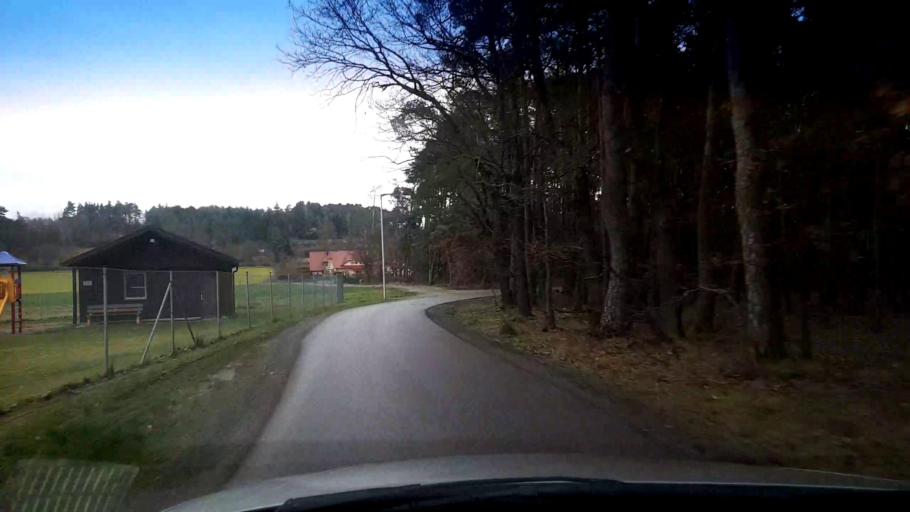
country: DE
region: Bavaria
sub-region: Upper Franconia
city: Oberhaid
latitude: 49.9358
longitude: 10.8033
